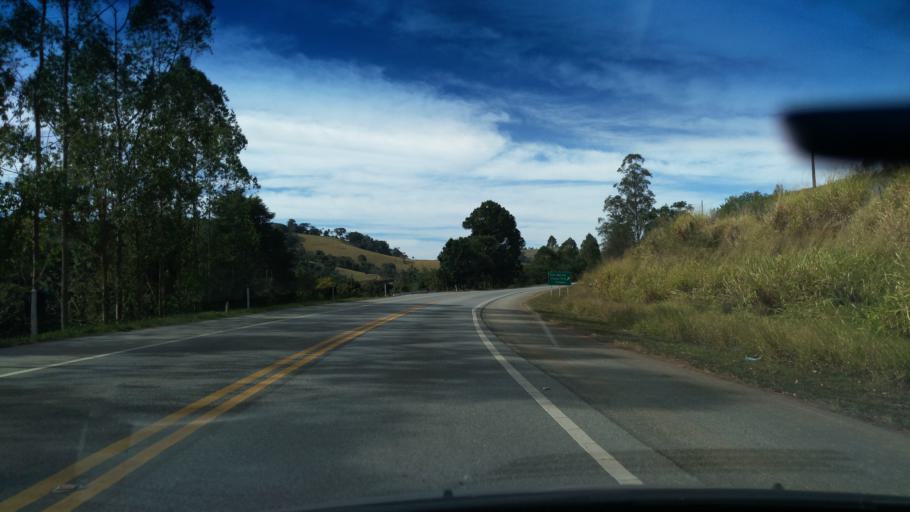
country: BR
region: Minas Gerais
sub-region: Borda Da Mata
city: Borda da Mata
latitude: -22.1397
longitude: -46.1379
